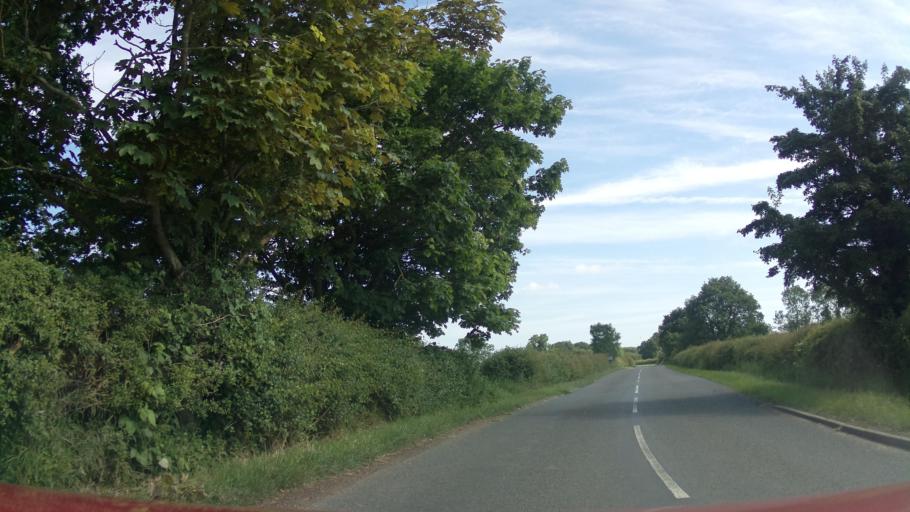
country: GB
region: England
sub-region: Lincolnshire
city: Skellingthorpe
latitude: 53.1478
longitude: -0.6331
